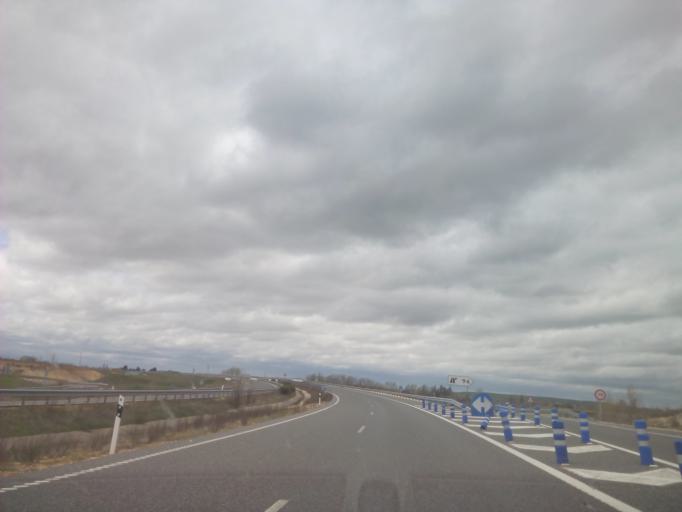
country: ES
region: Castille and Leon
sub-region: Provincia de Salamanca
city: Pelabravo
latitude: 40.9427
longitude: -5.5966
